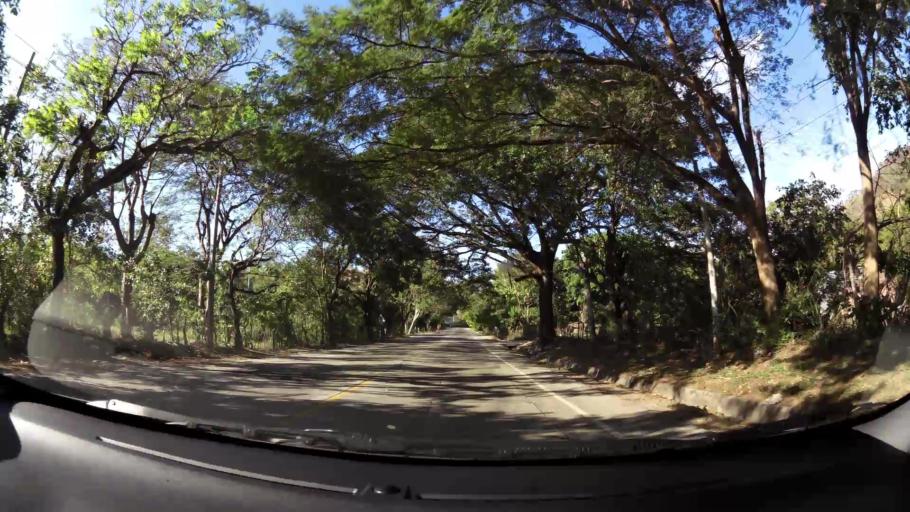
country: SV
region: Santa Ana
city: Texistepeque
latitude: 14.1122
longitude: -89.4988
